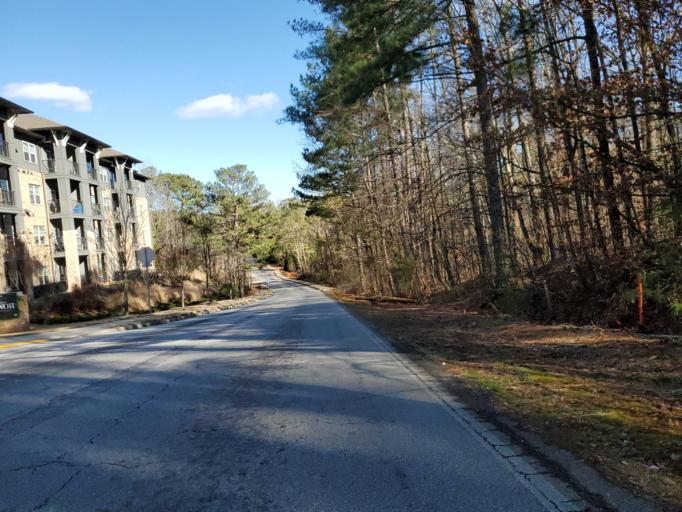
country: US
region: Georgia
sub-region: DeKalb County
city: Avondale Estates
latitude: 33.7709
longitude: -84.2308
